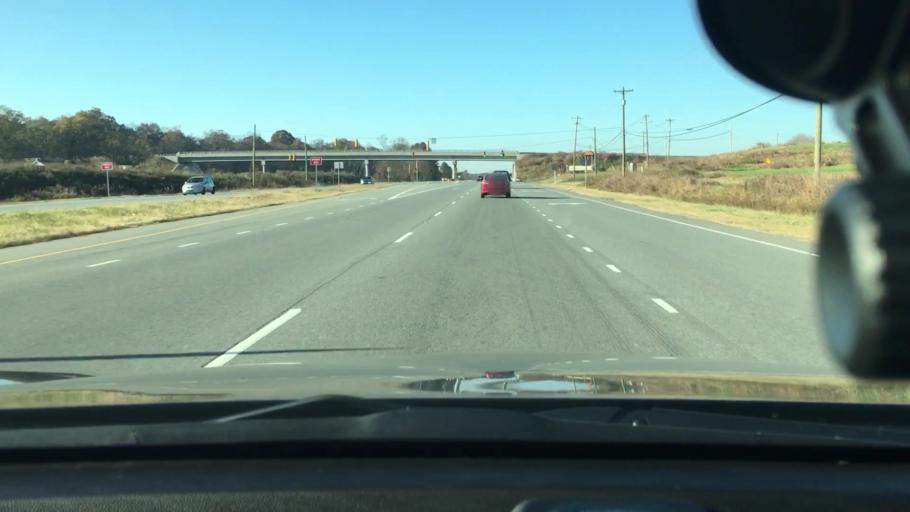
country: US
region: North Carolina
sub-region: Cabarrus County
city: Harrisburg
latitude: 35.3383
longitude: -80.6172
